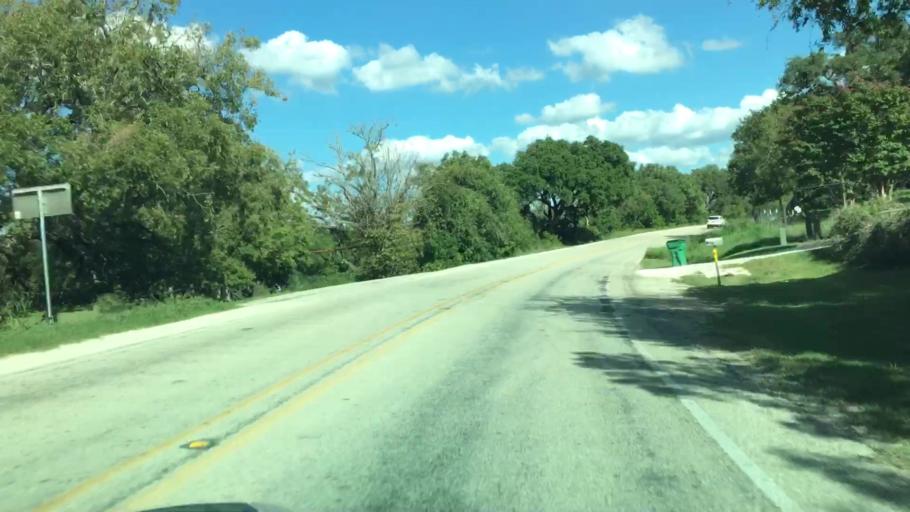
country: US
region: Texas
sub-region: Blanco County
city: Blanco
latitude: 30.0932
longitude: -98.4087
